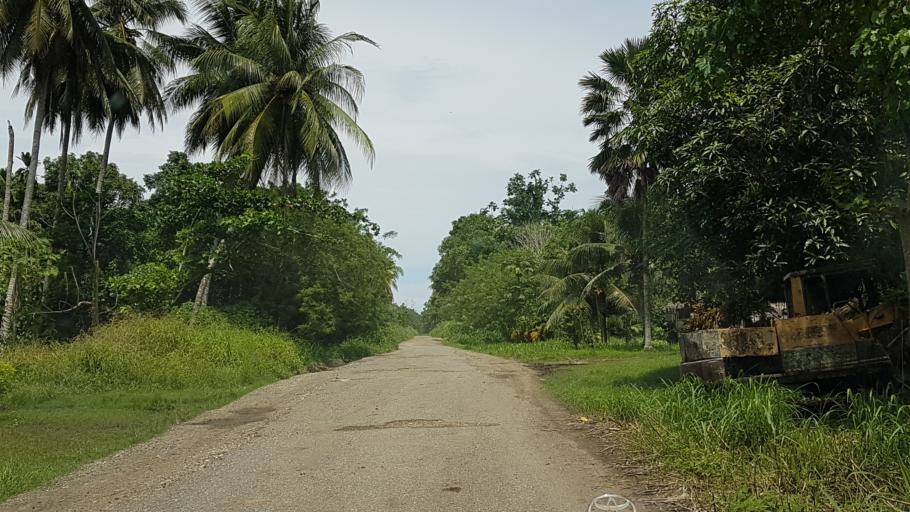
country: PG
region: Madang
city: Madang
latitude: -4.5664
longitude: 145.5067
